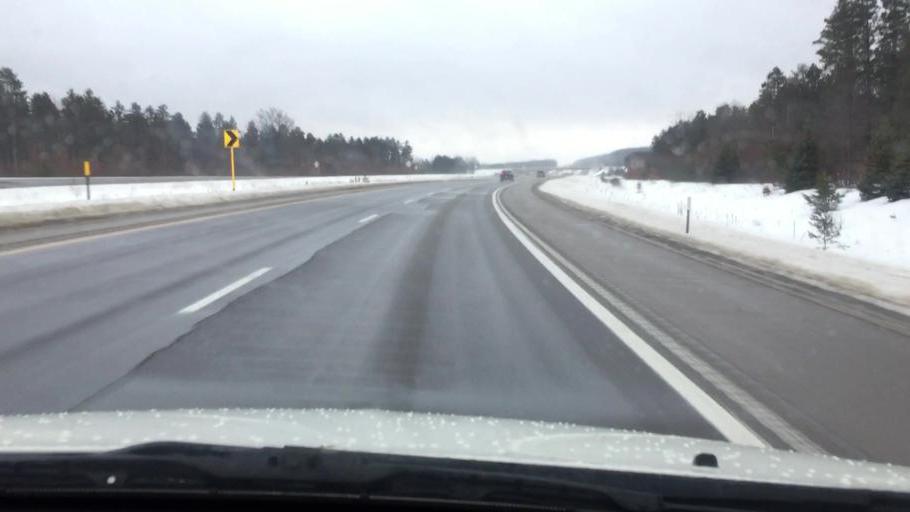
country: US
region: Michigan
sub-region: Wexford County
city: Manton
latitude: 44.4624
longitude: -85.3960
